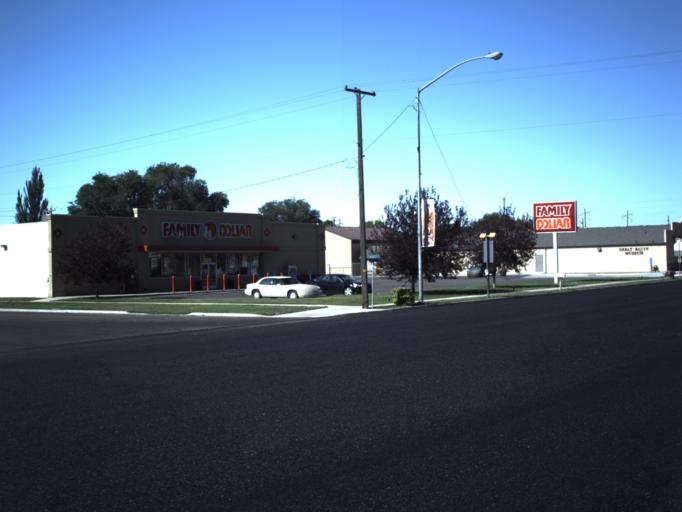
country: US
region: Utah
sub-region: Millard County
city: Delta
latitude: 39.3525
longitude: -112.5746
